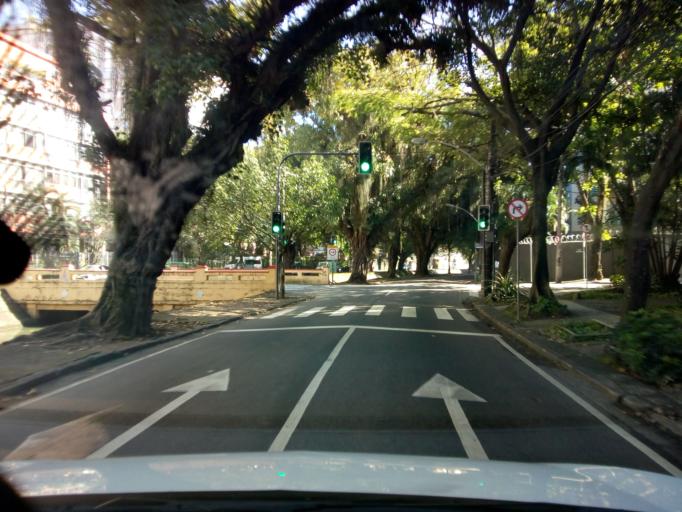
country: BR
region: Rio de Janeiro
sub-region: Rio De Janeiro
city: Rio de Janeiro
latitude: -22.9852
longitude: -43.2293
